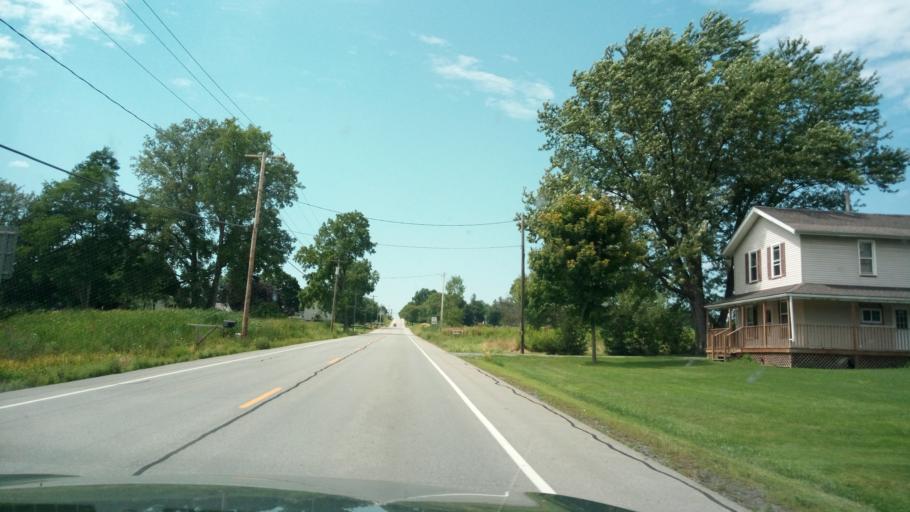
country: US
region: New York
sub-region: Livingston County
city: Geneseo
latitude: 42.8309
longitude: -77.9024
